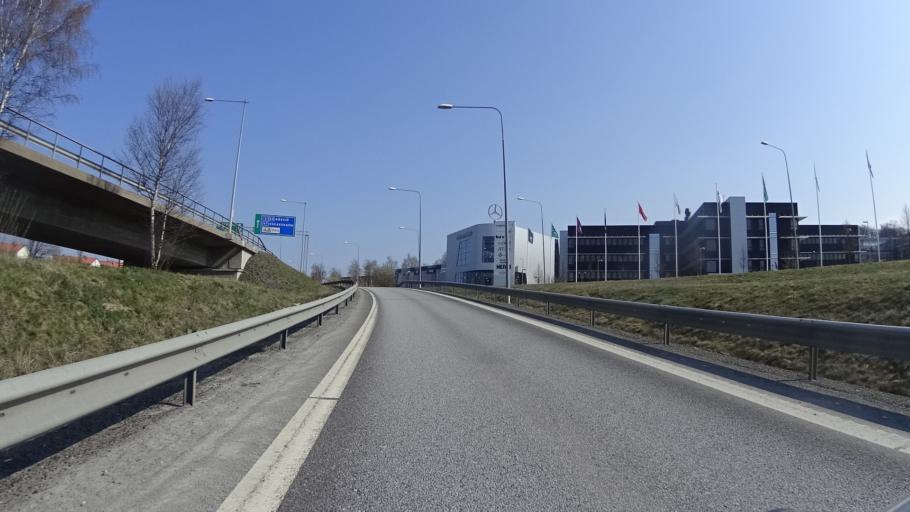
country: SE
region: Joenkoeping
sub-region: Jonkopings Kommun
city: Jonkoping
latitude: 57.7746
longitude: 14.2094
